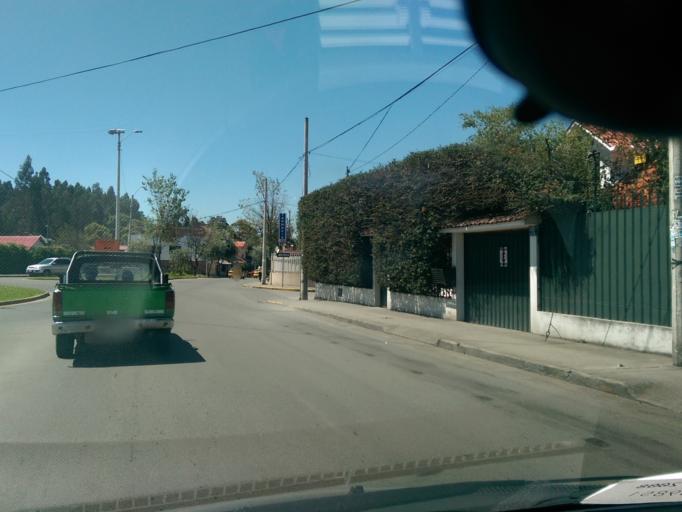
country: EC
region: Azuay
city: Cuenca
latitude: -2.9105
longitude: -79.0198
